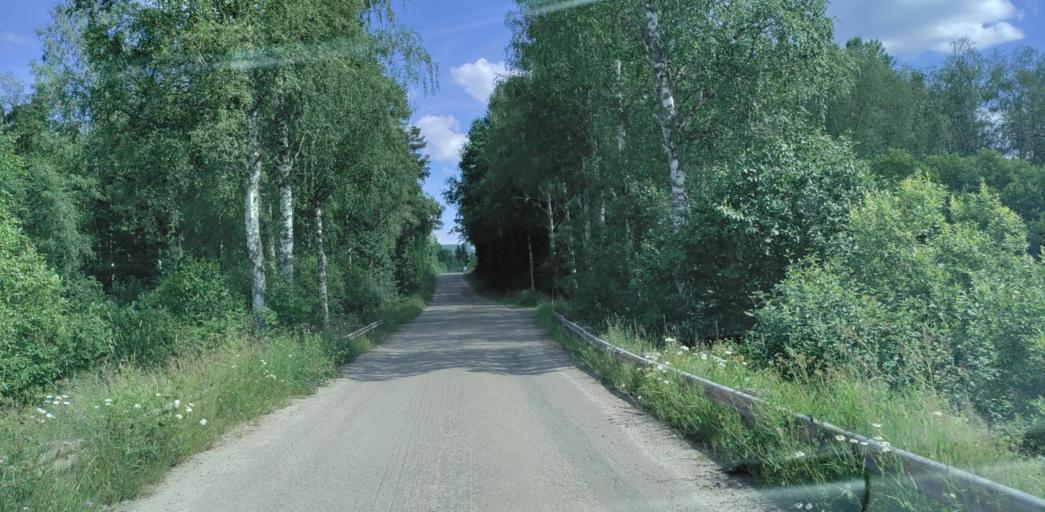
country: SE
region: Vaermland
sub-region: Hagfors Kommun
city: Ekshaerad
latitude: 60.1278
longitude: 13.4709
